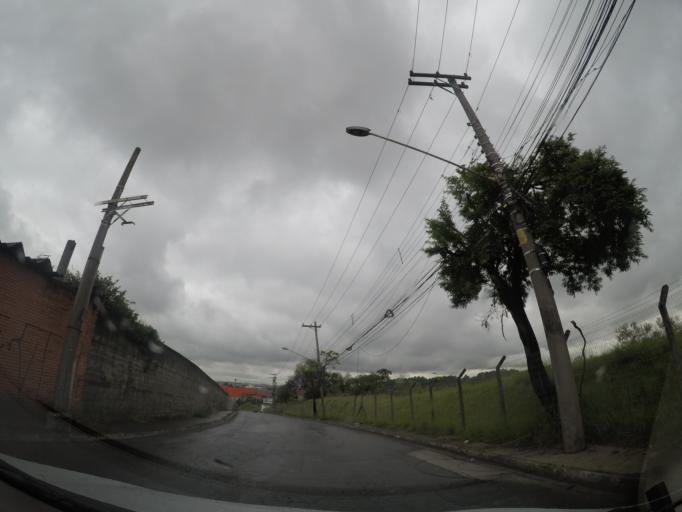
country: BR
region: Sao Paulo
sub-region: Guarulhos
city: Guarulhos
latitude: -23.4742
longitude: -46.4452
